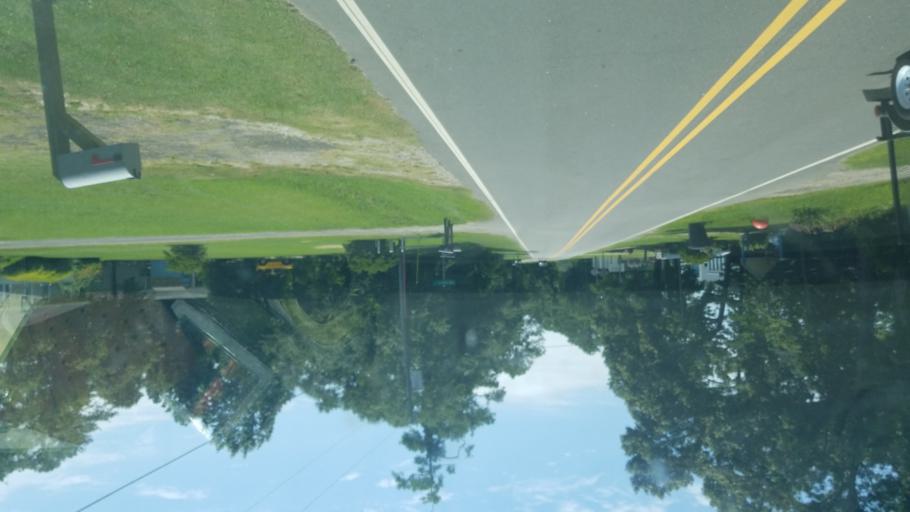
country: US
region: North Carolina
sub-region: Dare County
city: Manteo
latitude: 35.8918
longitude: -75.7678
